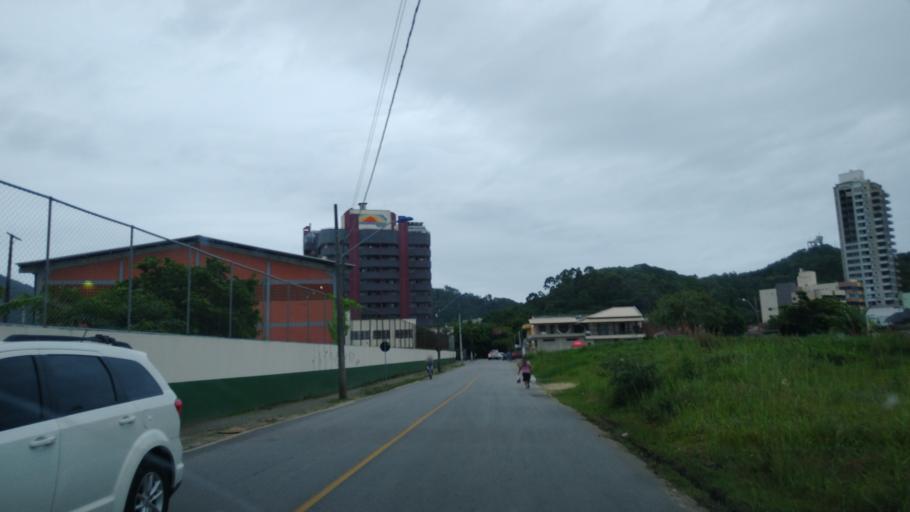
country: BR
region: Santa Catarina
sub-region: Itapema
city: Itapema
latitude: -27.0924
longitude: -48.6117
